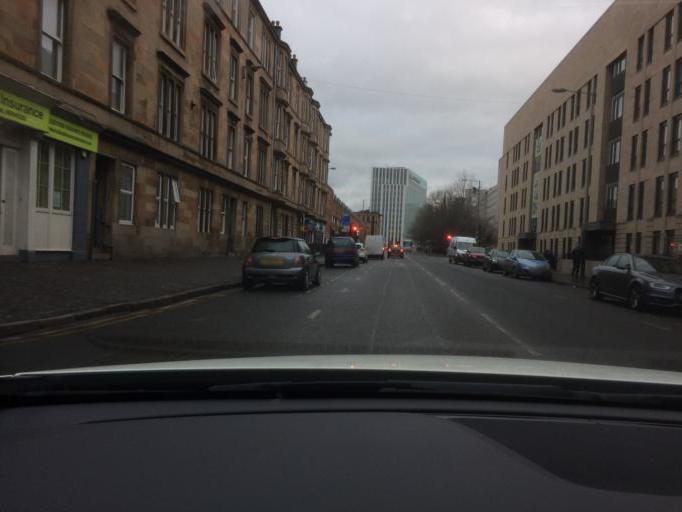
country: GB
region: Scotland
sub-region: Glasgow City
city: Glasgow
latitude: 55.8630
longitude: -4.2769
